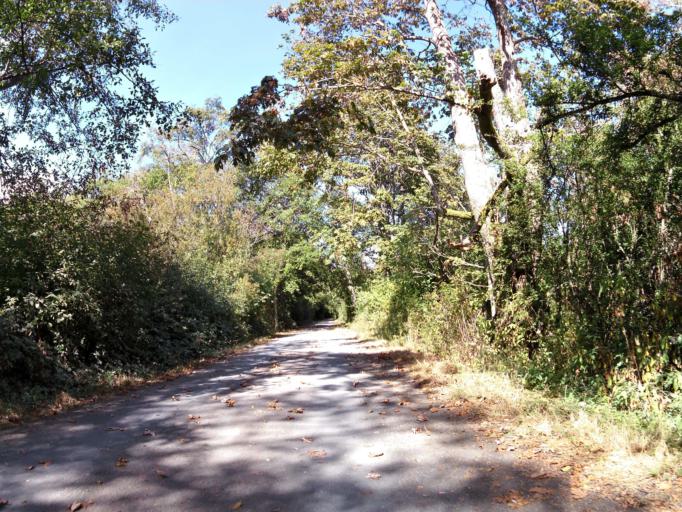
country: CA
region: British Columbia
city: Victoria
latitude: 48.5431
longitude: -123.3833
